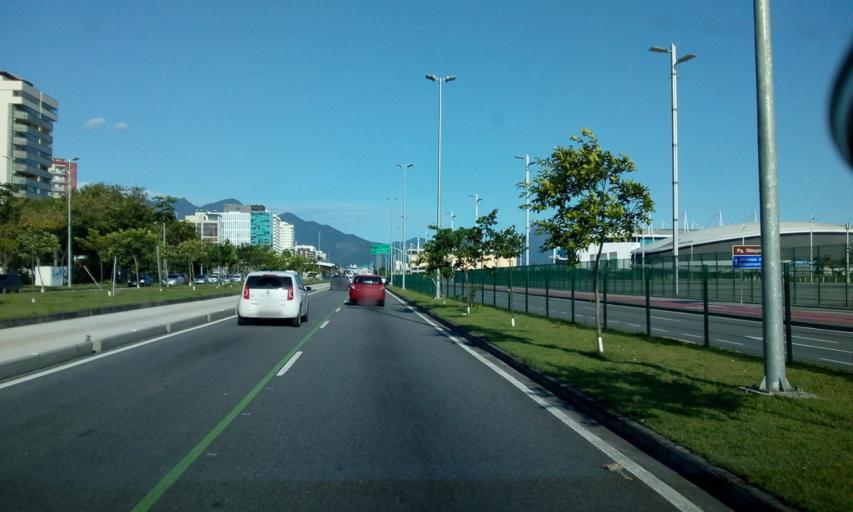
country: BR
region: Rio de Janeiro
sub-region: Nilopolis
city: Nilopolis
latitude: -22.9733
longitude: -43.3958
